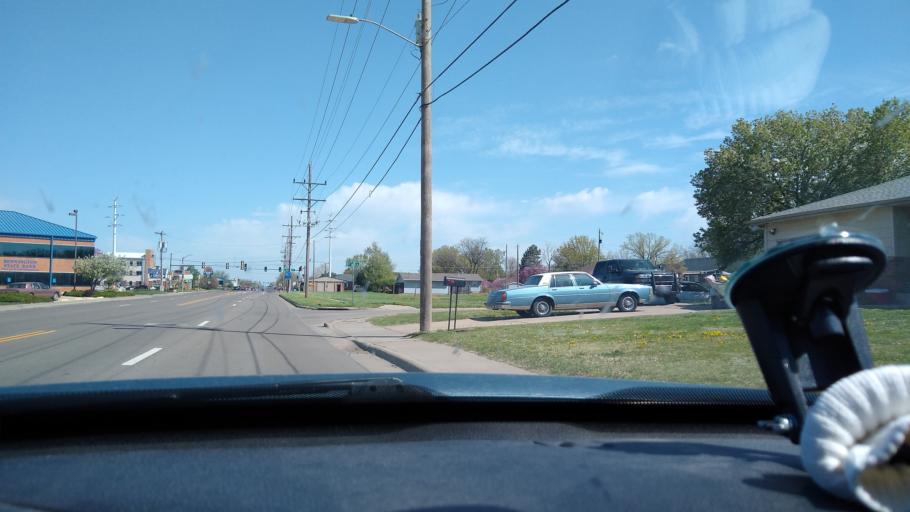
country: US
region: Kansas
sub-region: Saline County
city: Salina
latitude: 38.8032
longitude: -97.5943
